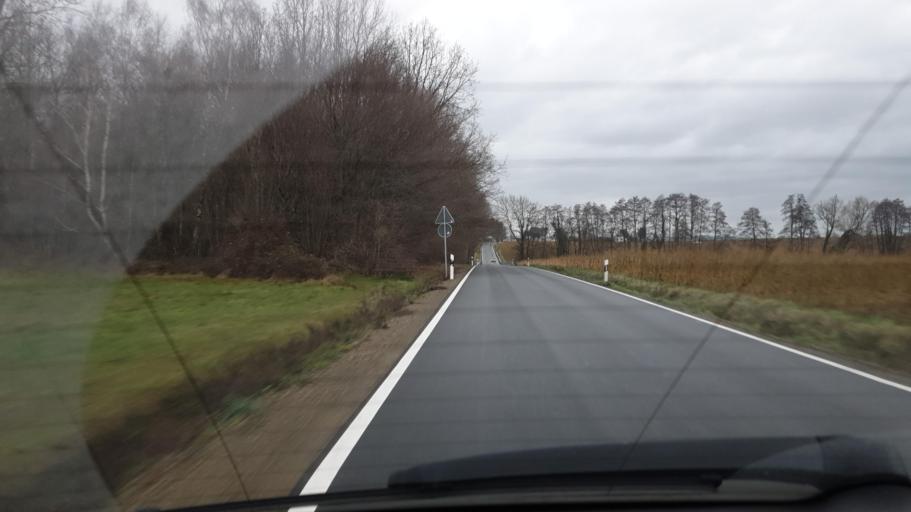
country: DE
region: North Rhine-Westphalia
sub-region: Regierungsbezirk Detmold
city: Lage
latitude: 51.9887
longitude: 8.8422
